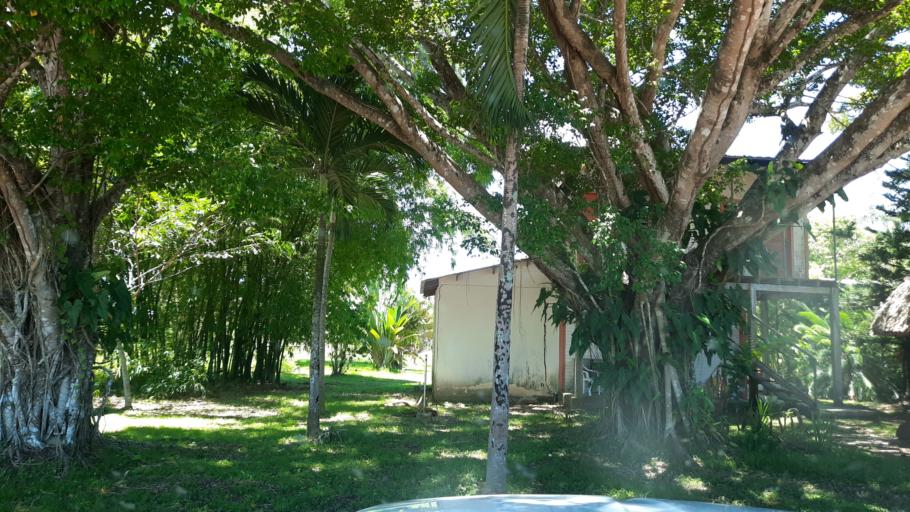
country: BZ
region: Cayo
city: Belmopan
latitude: 17.3237
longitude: -88.5648
